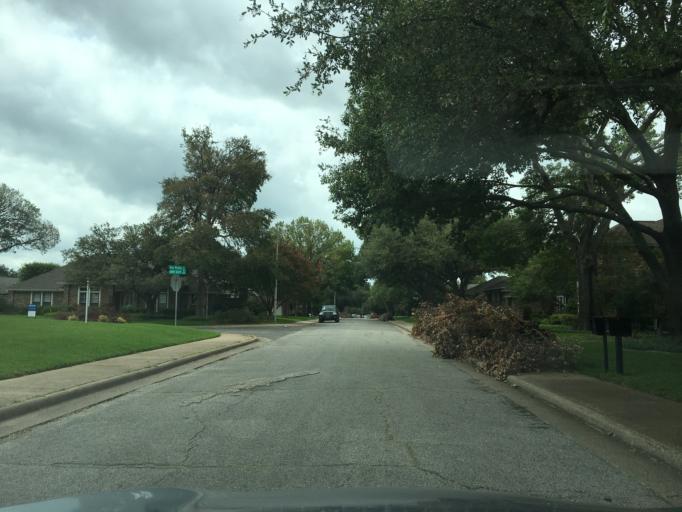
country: US
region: Texas
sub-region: Dallas County
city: Richardson
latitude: 32.9059
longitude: -96.7416
